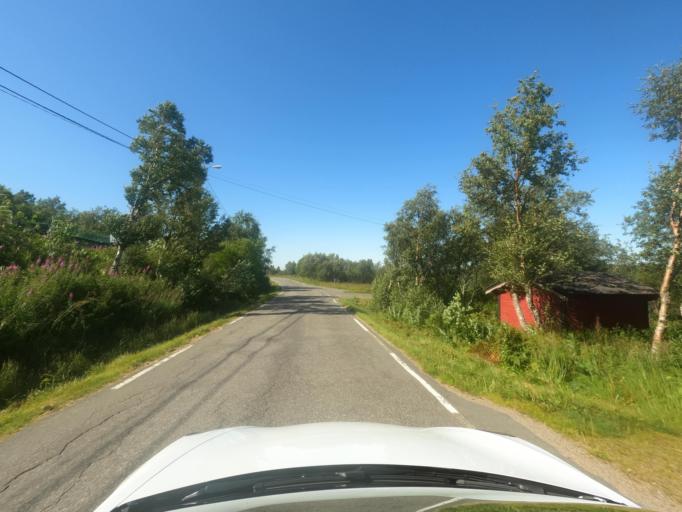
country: NO
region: Nordland
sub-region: Hadsel
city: Melbu
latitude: 68.4342
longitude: 14.7537
